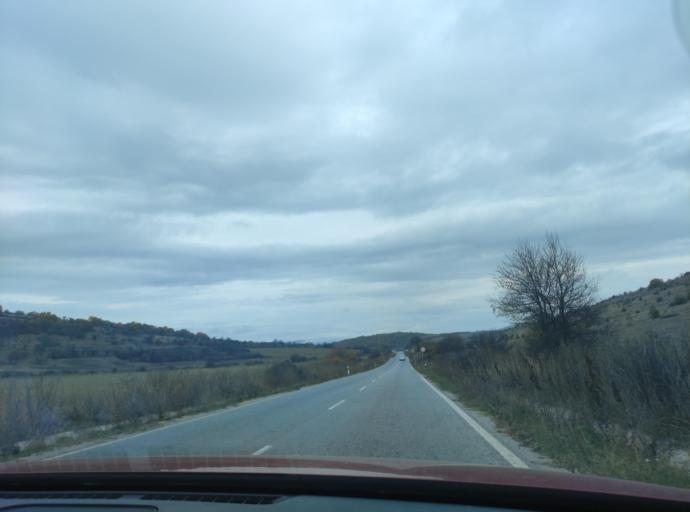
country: BG
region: Sofiya
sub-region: Obshtina Godech
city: Godech
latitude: 42.9549
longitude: 23.1568
